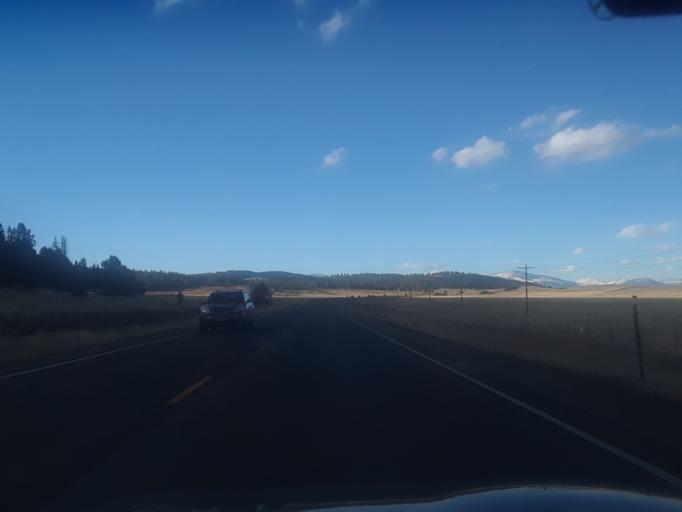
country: US
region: Colorado
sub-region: Park County
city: Fairplay
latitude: 39.0134
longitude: -105.9717
